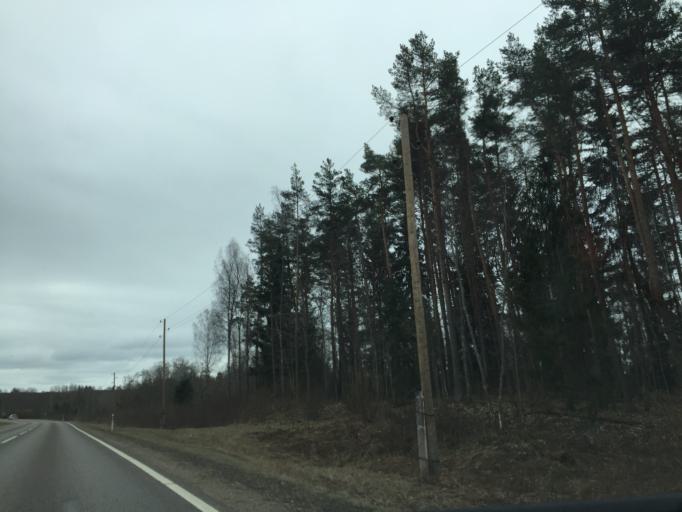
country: LV
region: Kraslavas Rajons
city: Kraslava
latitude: 55.9118
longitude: 27.0025
